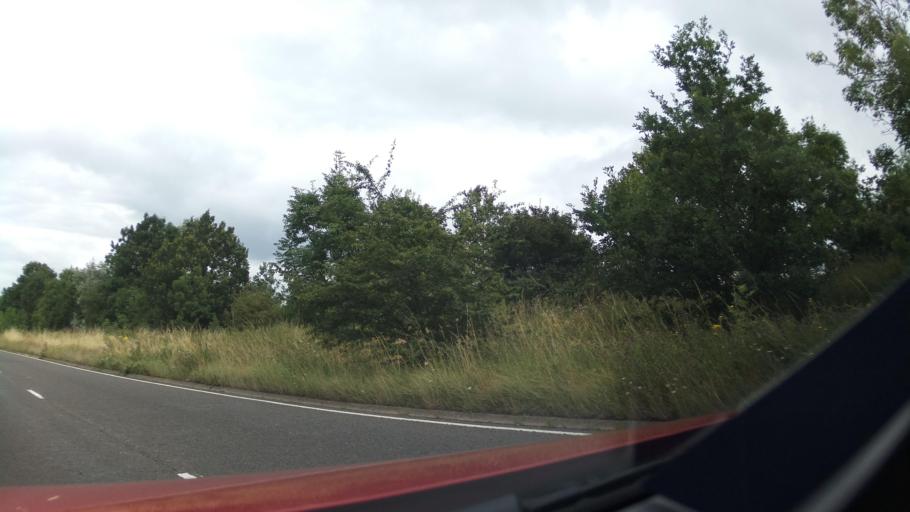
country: GB
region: England
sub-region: Northamptonshire
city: Geddington
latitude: 52.4467
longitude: -0.7351
